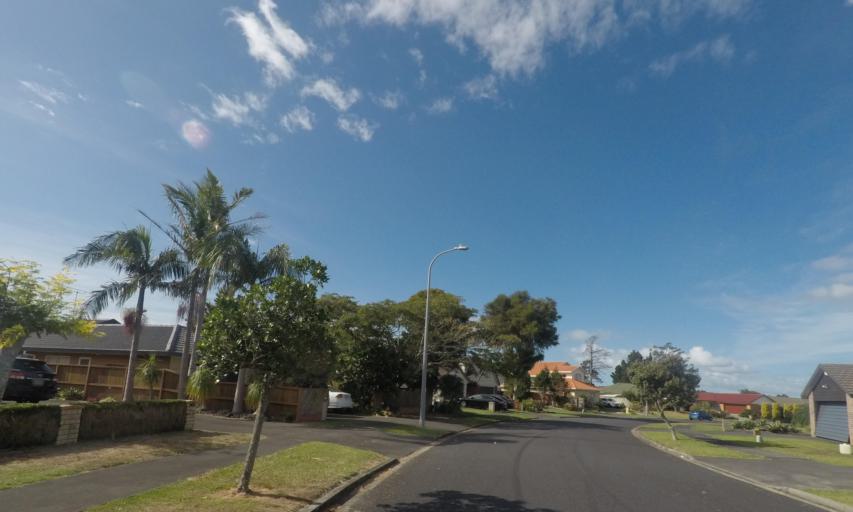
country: NZ
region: Auckland
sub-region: Auckland
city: Pakuranga
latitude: -36.9224
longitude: 174.8920
